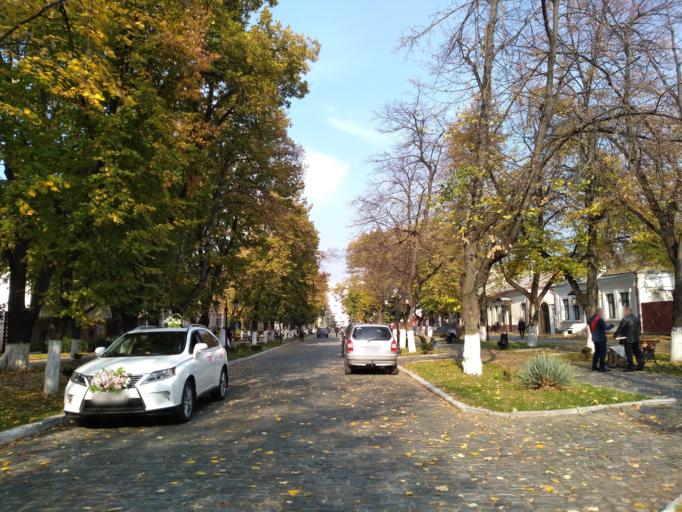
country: MD
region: Bender
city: Bender
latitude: 46.8216
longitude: 29.4813
